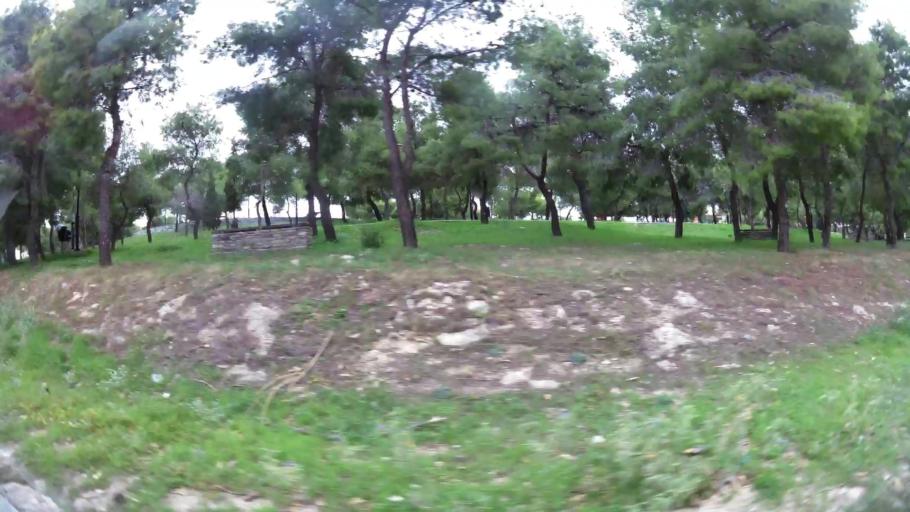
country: GR
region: Attica
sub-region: Nomarchia Athinas
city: Alimos
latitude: 37.9106
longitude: 23.7229
